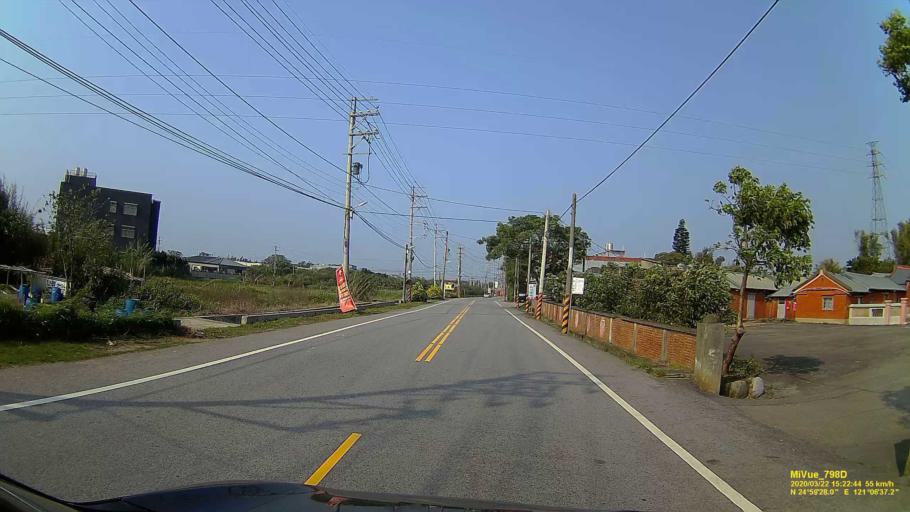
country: TW
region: Taiwan
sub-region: Hsinchu
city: Zhubei
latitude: 24.9913
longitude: 121.1105
